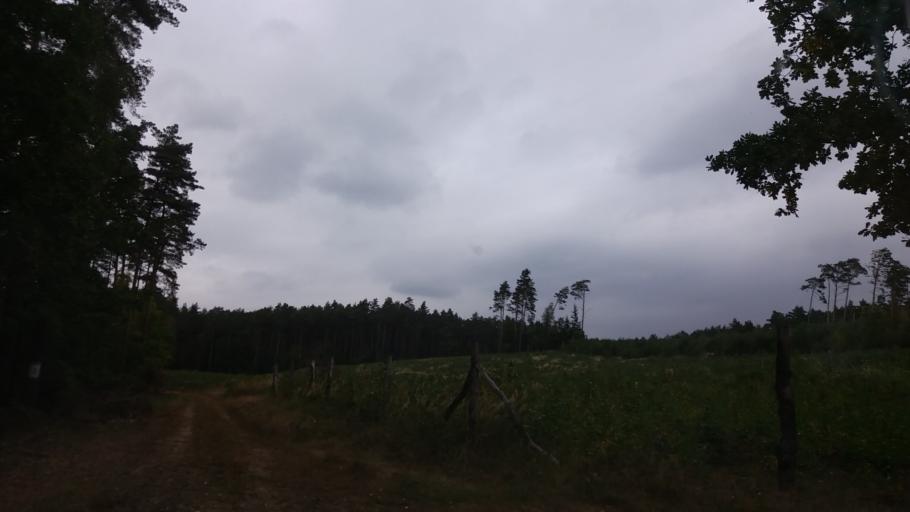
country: PL
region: West Pomeranian Voivodeship
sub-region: Powiat choszczenski
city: Bierzwnik
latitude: 52.9842
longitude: 15.6109
